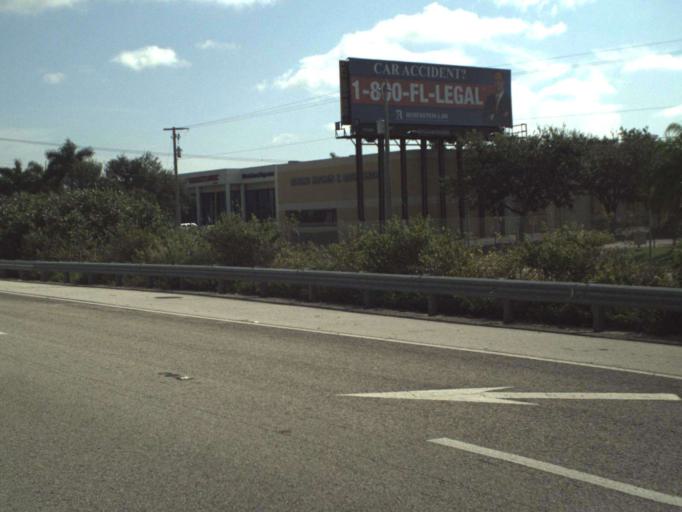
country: US
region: Florida
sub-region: Palm Beach County
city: North Palm Beach
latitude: 26.7898
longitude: -80.0987
